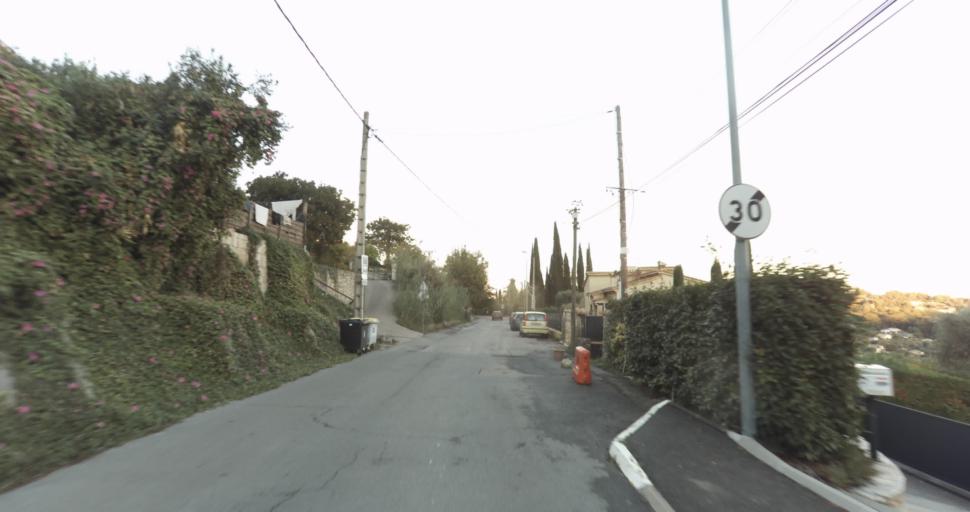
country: FR
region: Provence-Alpes-Cote d'Azur
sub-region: Departement des Alpes-Maritimes
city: Vence
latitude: 43.7315
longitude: 7.1202
